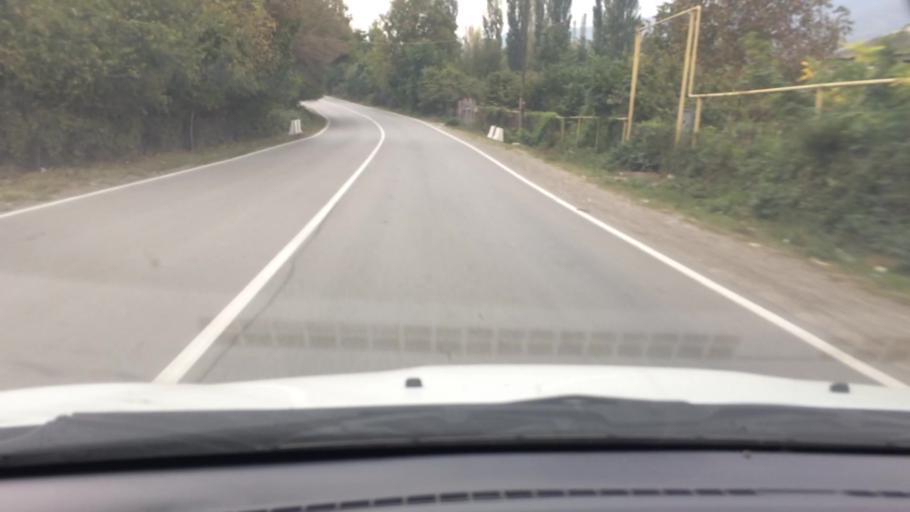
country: AM
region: Tavush
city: Bagratashen
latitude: 41.2345
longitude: 44.8105
